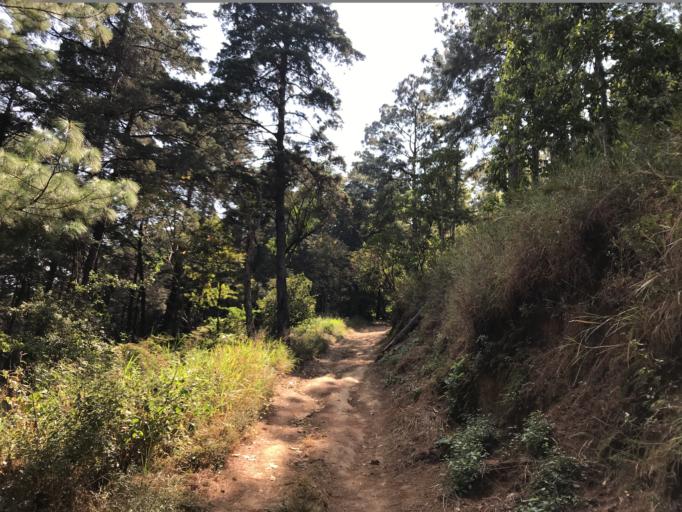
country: GT
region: Guatemala
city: Villa Canales
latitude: 14.4828
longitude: -90.5516
